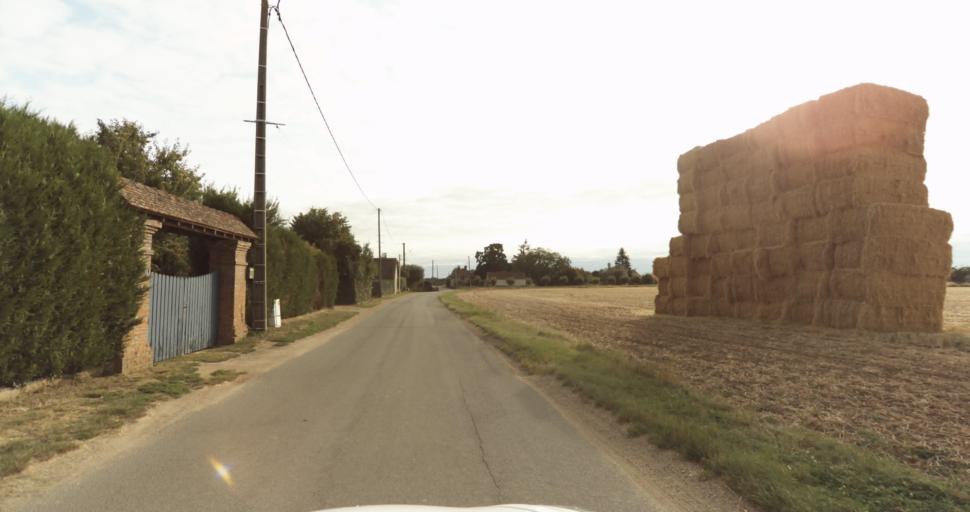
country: FR
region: Centre
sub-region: Departement d'Eure-et-Loir
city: Saint-Remy-sur-Avre
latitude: 48.8182
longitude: 1.2413
